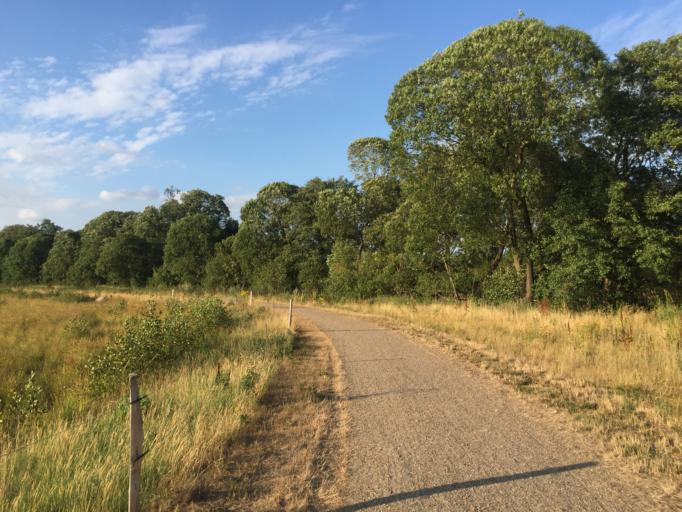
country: DK
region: South Denmark
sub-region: Odense Kommune
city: Hojby
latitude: 55.3514
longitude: 10.4318
